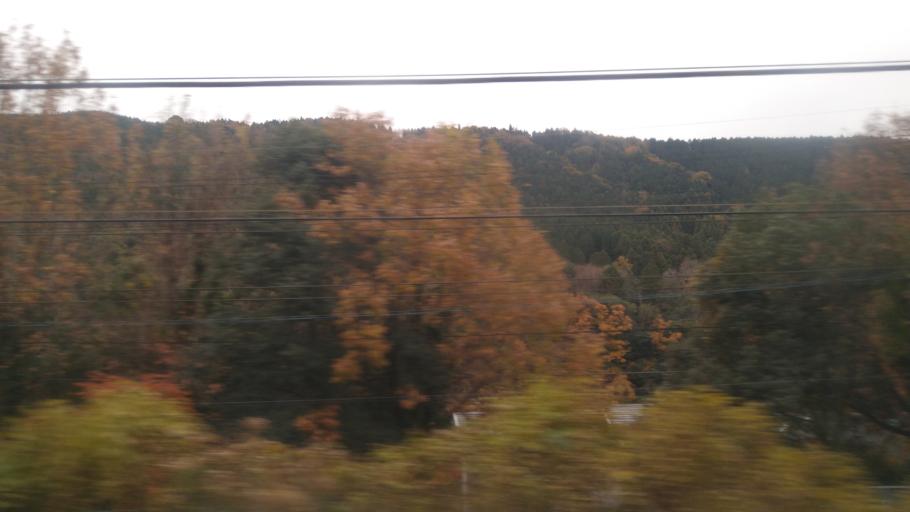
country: JP
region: Aichi
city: Seto
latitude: 35.2716
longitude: 137.0768
